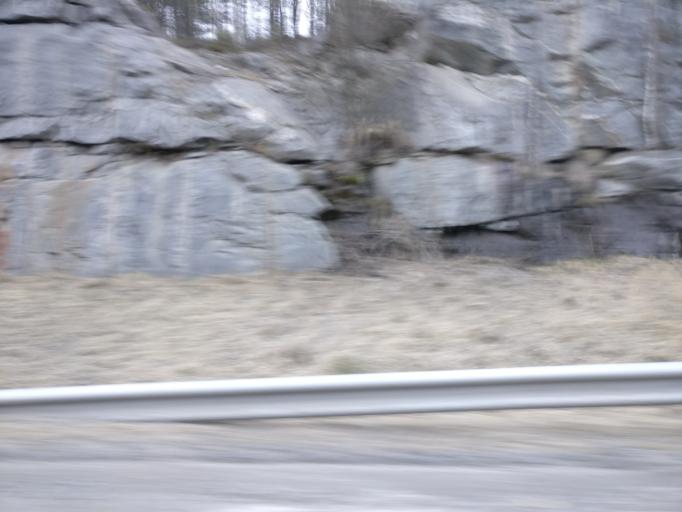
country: FI
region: Pirkanmaa
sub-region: Tampere
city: Tampere
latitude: 61.4618
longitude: 23.7797
